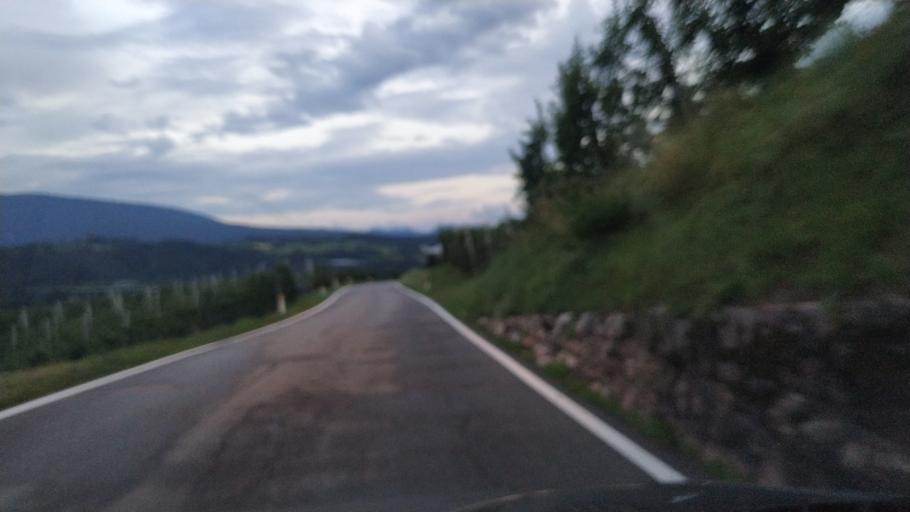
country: IT
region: Trentino-Alto Adige
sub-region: Provincia di Trento
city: Brez
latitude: 46.4404
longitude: 11.1112
